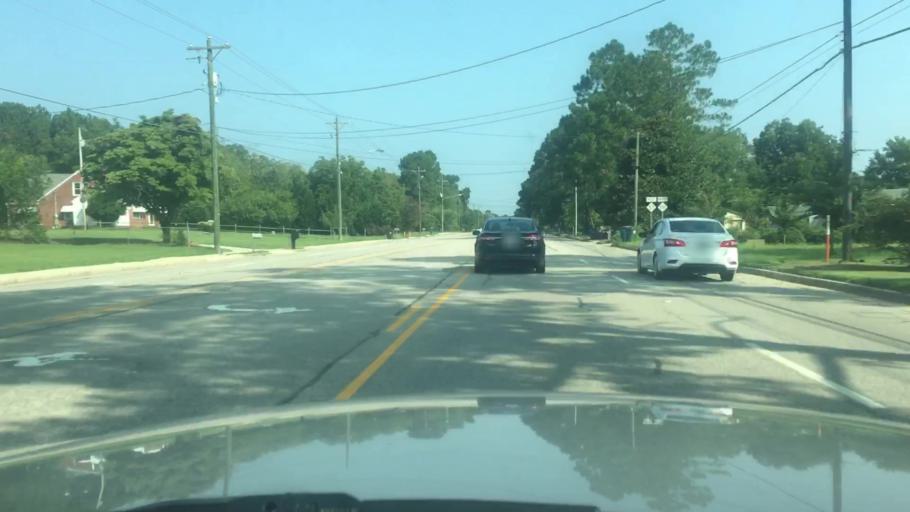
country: US
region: North Carolina
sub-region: Cumberland County
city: Vander
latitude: 35.0172
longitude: -78.8384
